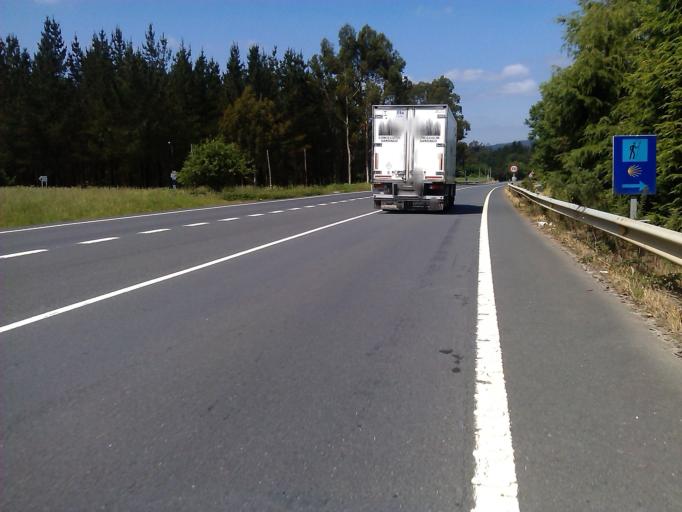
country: ES
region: Galicia
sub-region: Provincia da Coruna
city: Touro
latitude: 42.9176
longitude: -8.3320
